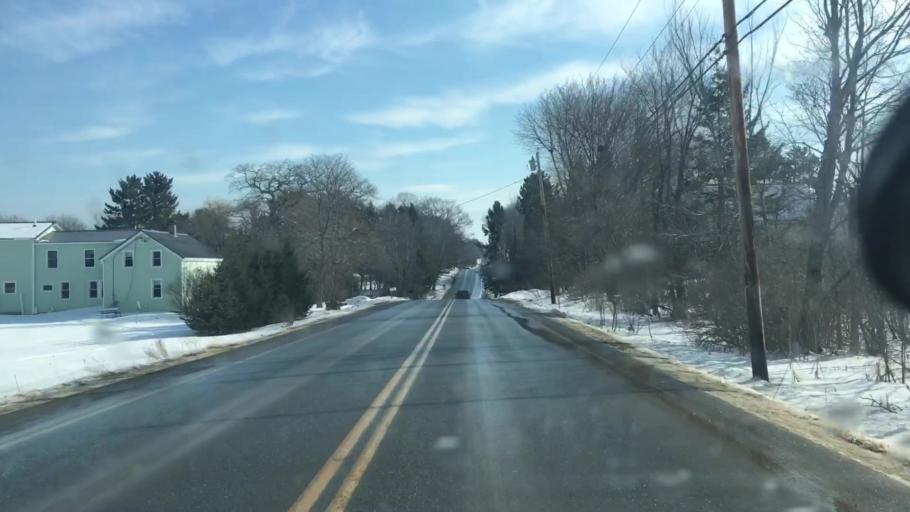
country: US
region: Maine
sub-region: Penobscot County
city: Bangor
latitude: 44.8450
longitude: -68.8357
